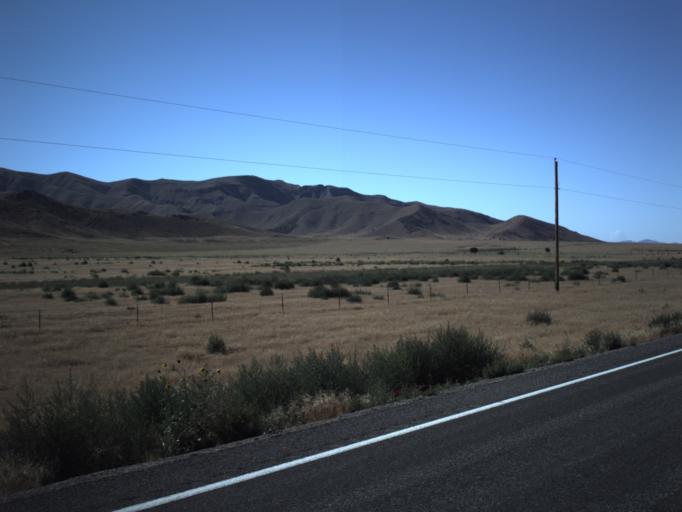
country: US
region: Utah
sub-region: Millard County
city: Delta
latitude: 39.6385
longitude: -112.3055
